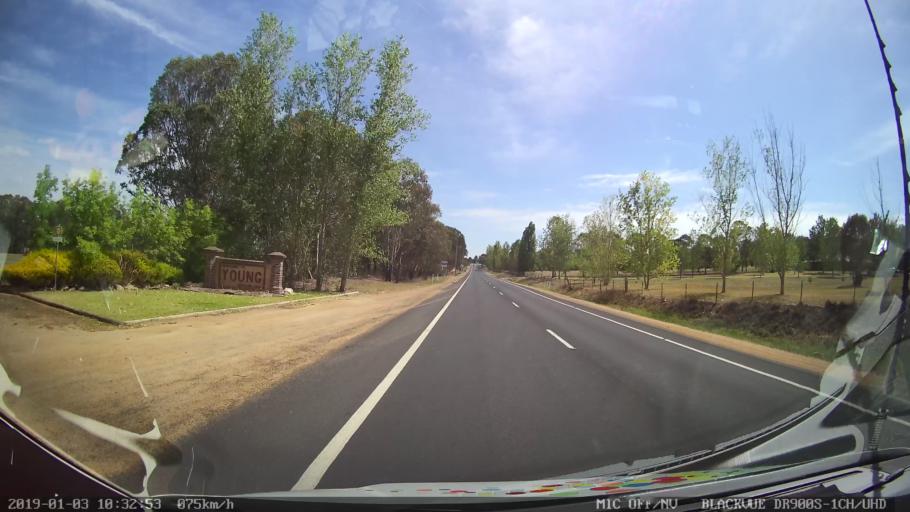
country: AU
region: New South Wales
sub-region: Young
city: Young
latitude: -34.3340
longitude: 148.2843
